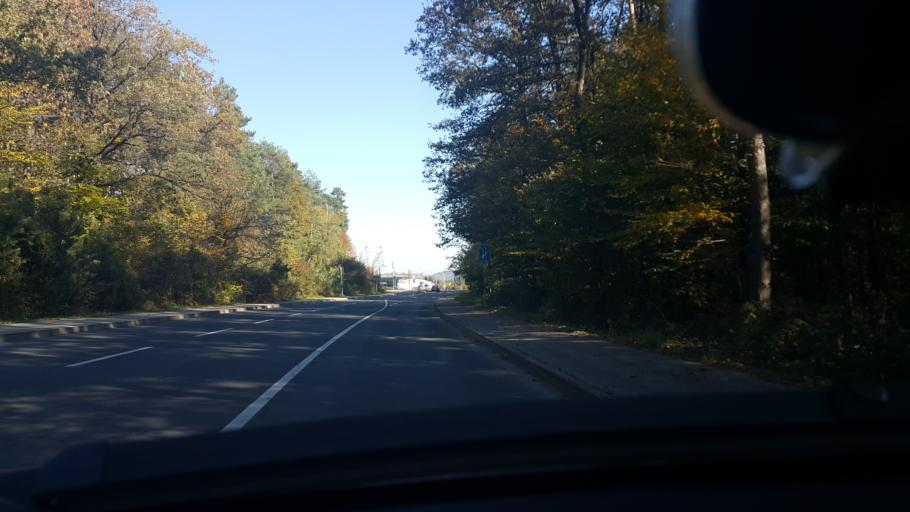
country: SI
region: Hoce-Slivnica
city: Rogoza
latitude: 46.5234
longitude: 15.6754
